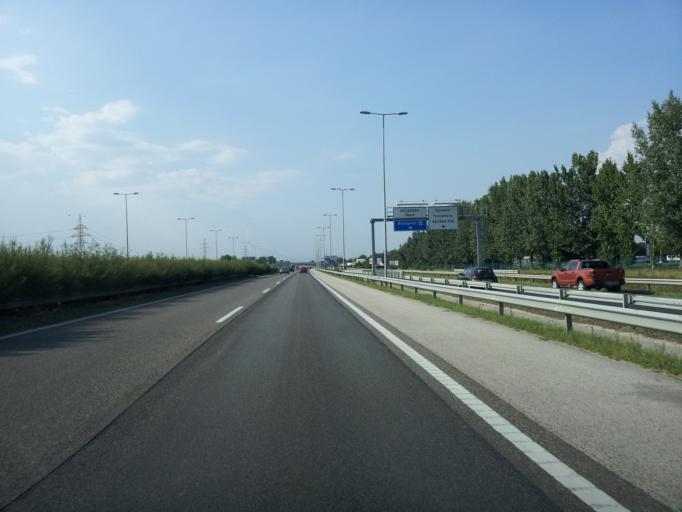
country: HU
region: Budapest
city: Budapest XVIII. keruelet
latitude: 47.4177
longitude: 19.1544
